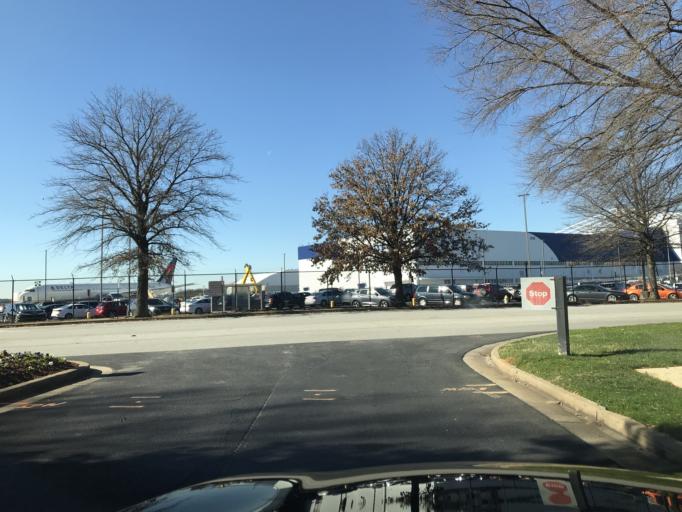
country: US
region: Georgia
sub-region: Fulton County
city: Hapeville
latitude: 33.6549
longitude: -84.4290
